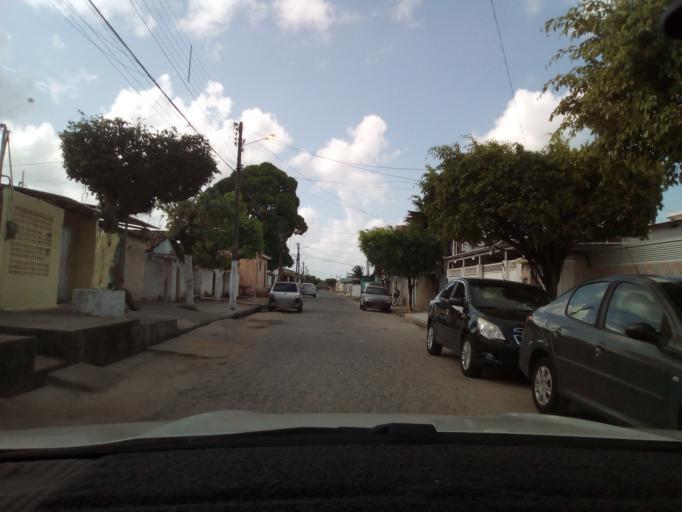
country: BR
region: Paraiba
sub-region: Bayeux
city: Bayeux
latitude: -7.1238
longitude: -34.9282
